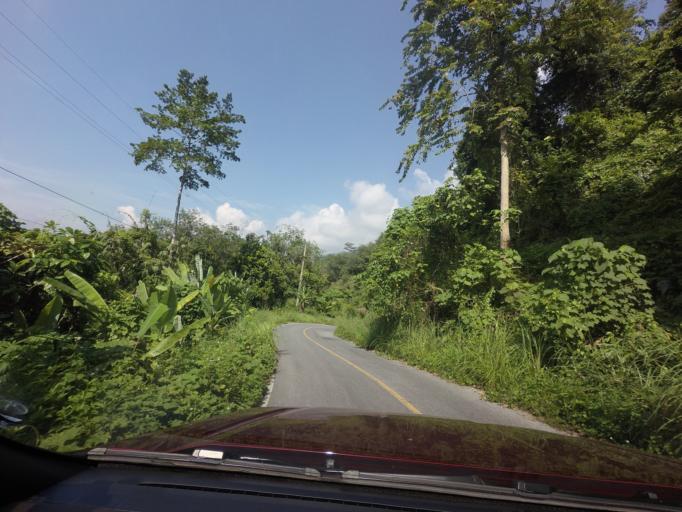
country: TH
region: Yala
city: Than To
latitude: 5.9895
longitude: 101.2024
